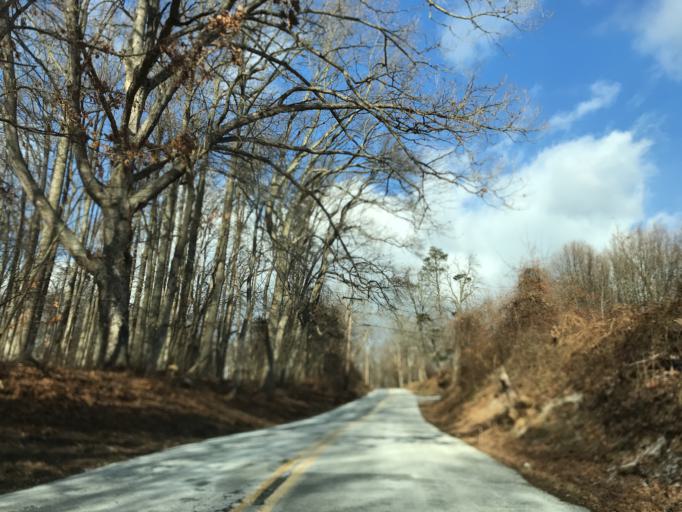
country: US
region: Maryland
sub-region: Baltimore County
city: Hunt Valley
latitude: 39.5797
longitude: -76.6553
